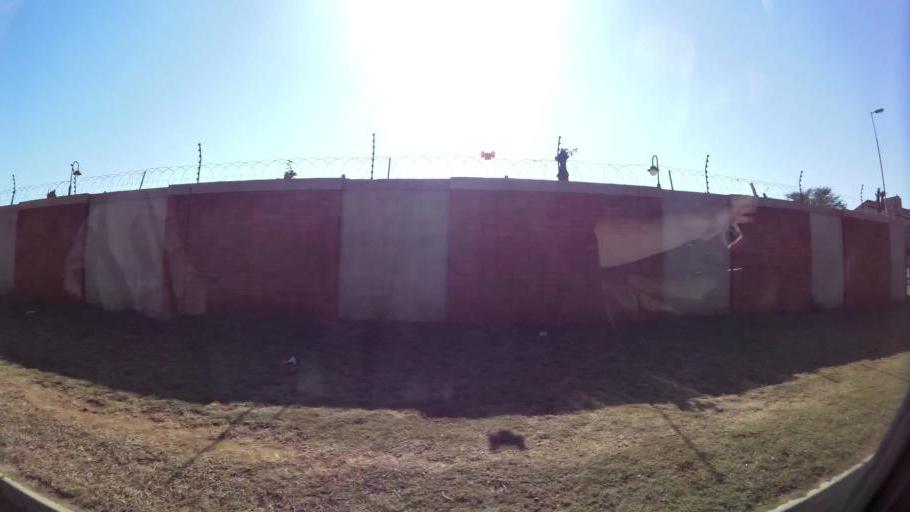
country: ZA
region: North-West
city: Ga-Rankuwa
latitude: -25.6518
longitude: 28.0842
